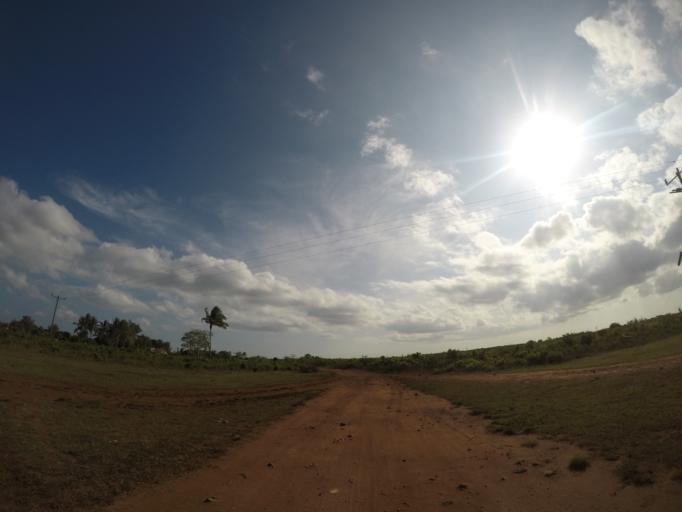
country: TZ
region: Zanzibar Central/South
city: Koani
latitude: -6.2048
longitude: 39.3154
